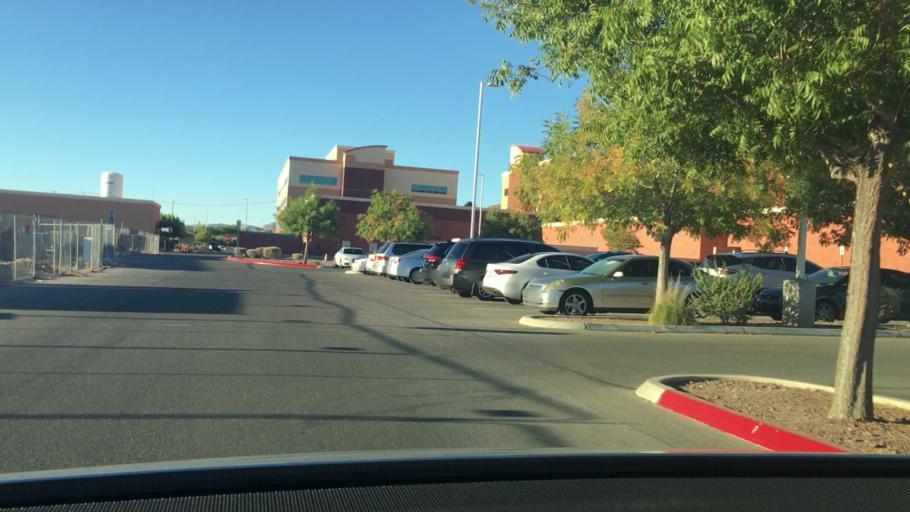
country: US
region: Nevada
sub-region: Clark County
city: Summerlin South
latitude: 36.0733
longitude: -115.2941
